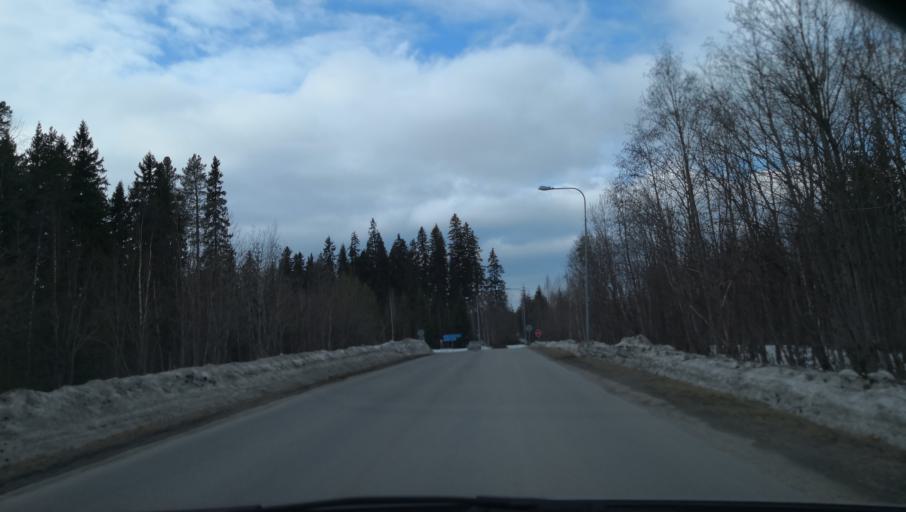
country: SE
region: Vaesterbotten
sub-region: Vannas Kommun
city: Vaennaes
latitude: 63.9183
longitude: 19.7400
